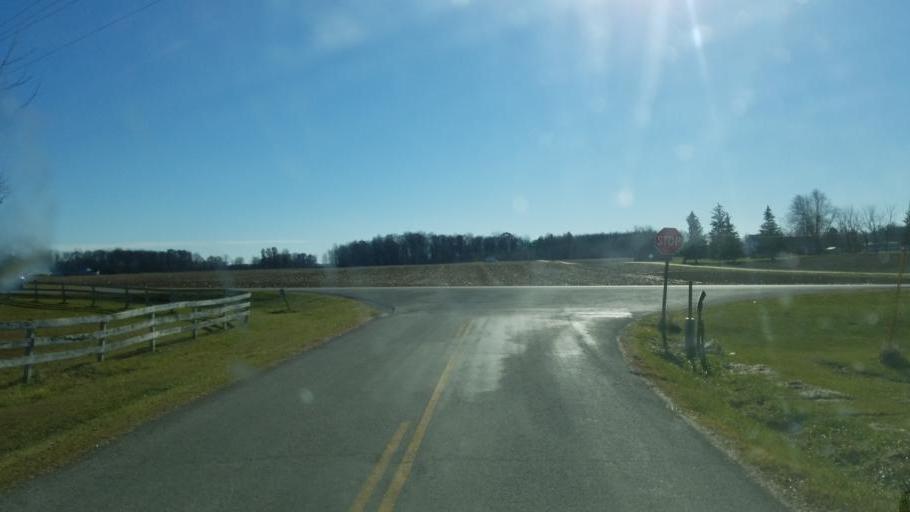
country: US
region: Ohio
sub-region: Crawford County
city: Galion
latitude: 40.8130
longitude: -82.8374
